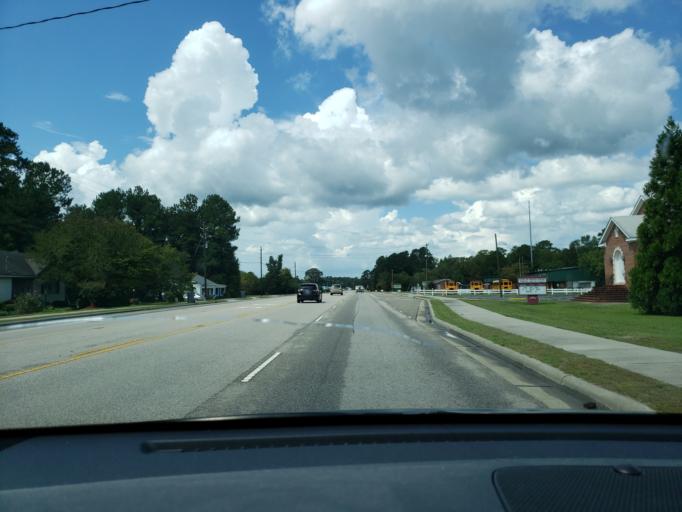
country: US
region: North Carolina
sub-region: Bladen County
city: Elizabethtown
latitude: 34.6540
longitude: -78.7187
